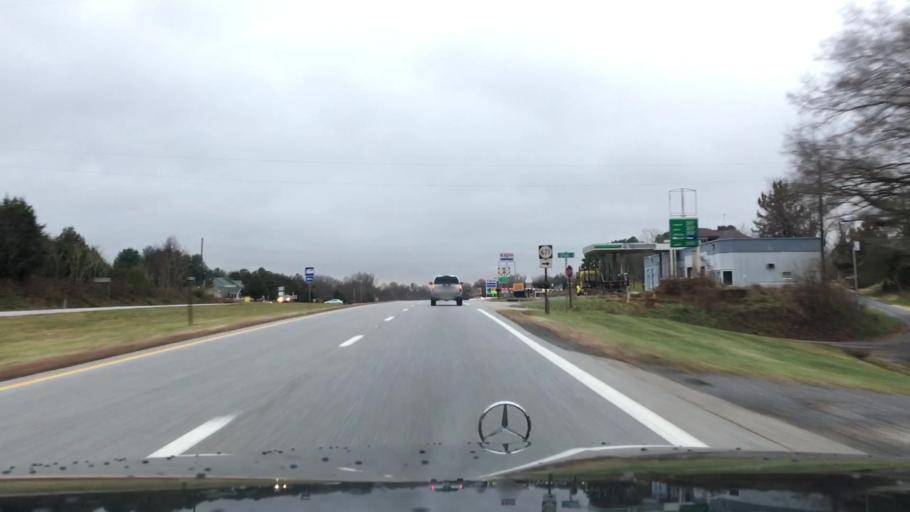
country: US
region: Virginia
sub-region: Nelson County
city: Lovingston
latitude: 37.7097
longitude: -78.9309
